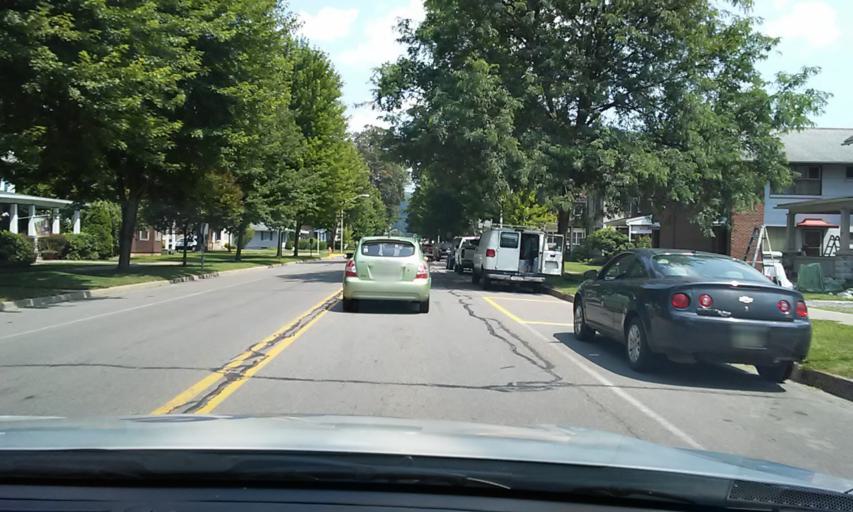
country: US
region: Pennsylvania
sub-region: Cameron County
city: Emporium
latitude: 41.5112
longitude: -78.2429
